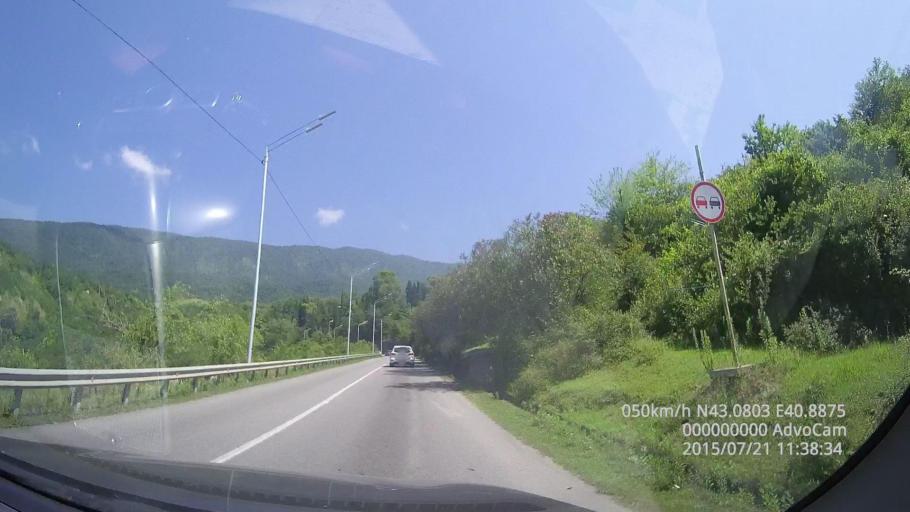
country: GE
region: Abkhazia
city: Stantsiya Novyy Afon
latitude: 43.0806
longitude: 40.8875
